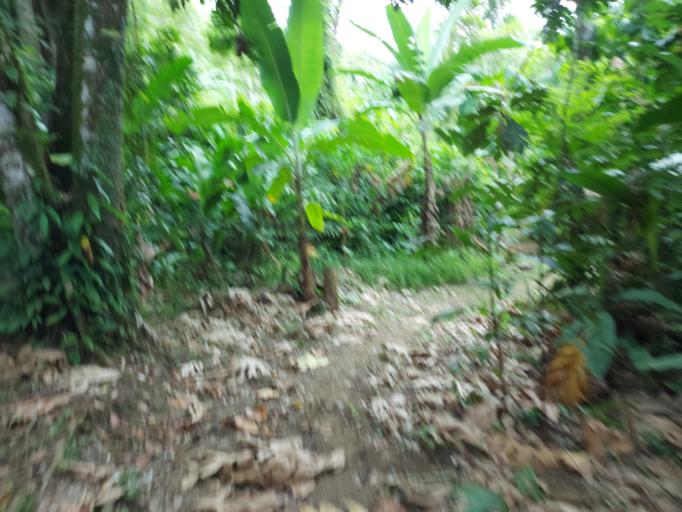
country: PA
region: Bocas del Toro
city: Barranco
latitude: 9.6436
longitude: -82.7862
